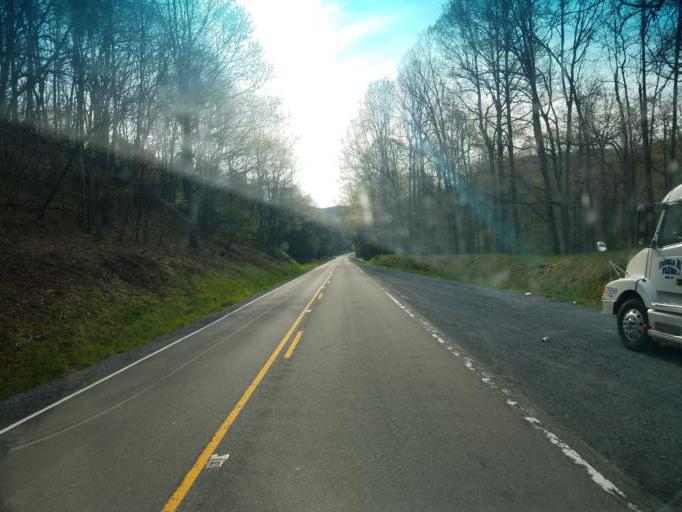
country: US
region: Virginia
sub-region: Smyth County
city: Atkins
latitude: 36.8109
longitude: -81.4126
